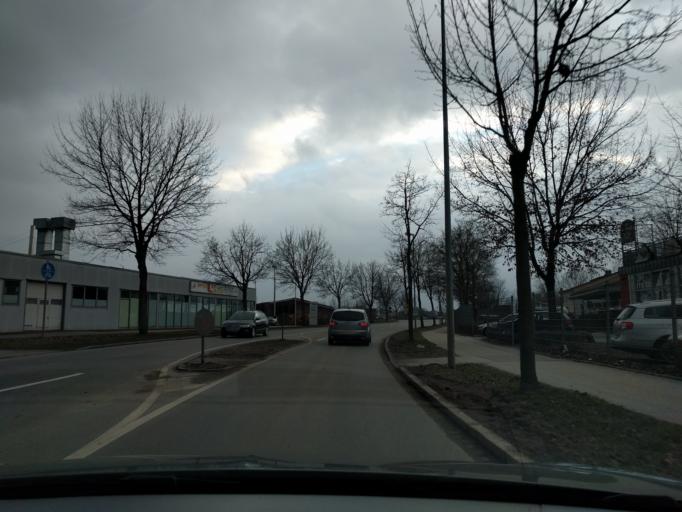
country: DE
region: Bavaria
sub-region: Lower Bavaria
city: Hengersberg
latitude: 48.7611
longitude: 13.0540
